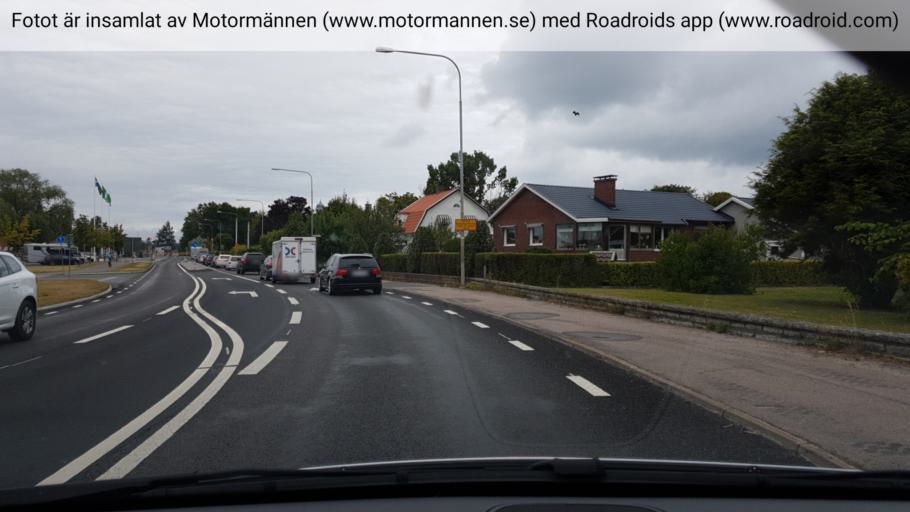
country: SE
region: Vaestra Goetaland
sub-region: Karlsborgs Kommun
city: Karlsborg
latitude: 58.5399
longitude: 14.5069
